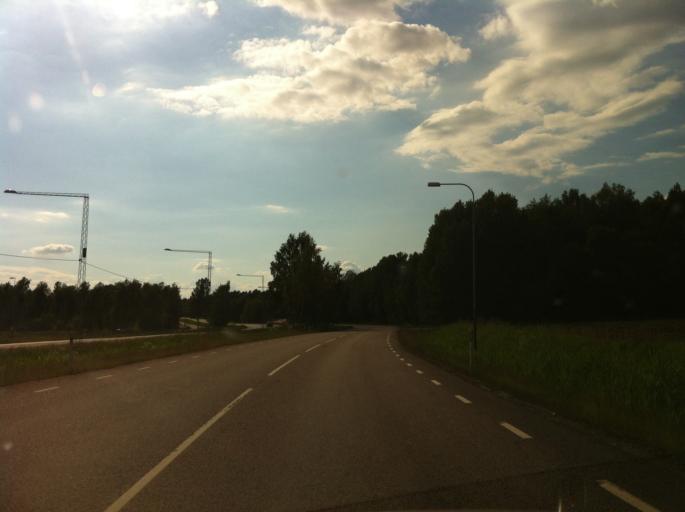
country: SE
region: Vaermland
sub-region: Karlstads Kommun
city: Karlstad
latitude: 59.4052
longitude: 13.4159
